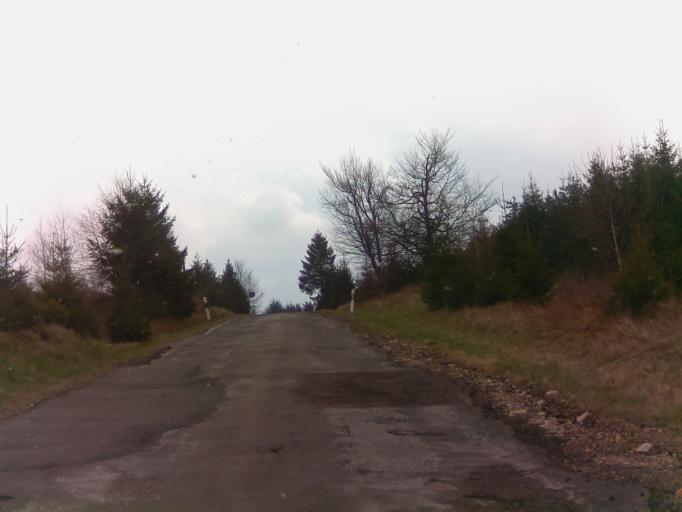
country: DE
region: Rheinland-Pfalz
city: Schauren
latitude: 49.8326
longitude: 7.2106
